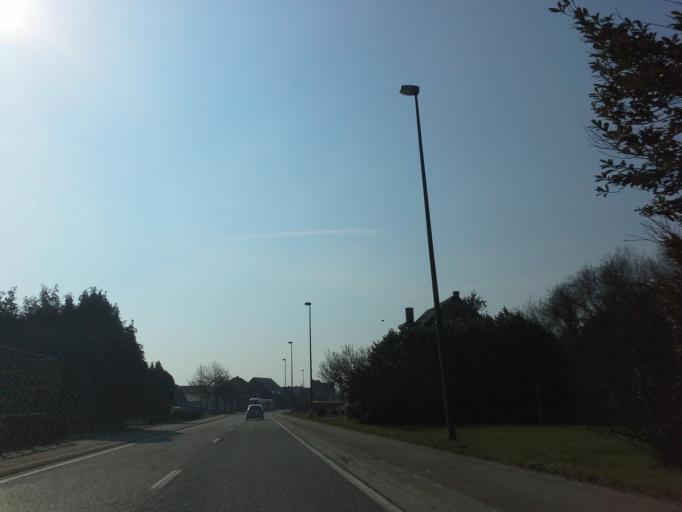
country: BE
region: Flanders
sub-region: Provincie Limburg
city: Tessenderlo
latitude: 51.0867
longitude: 5.1065
